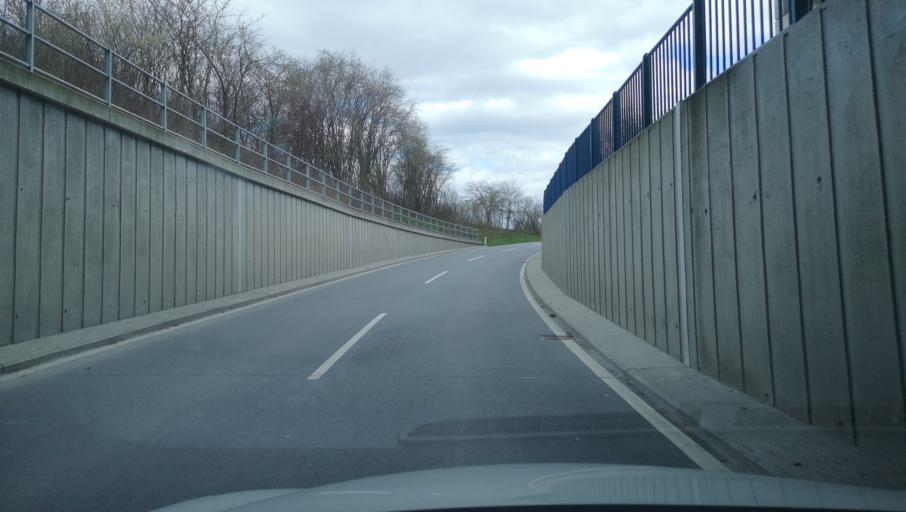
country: AT
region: Lower Austria
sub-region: Politischer Bezirk Melk
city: Blindenmarkt
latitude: 48.1251
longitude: 14.9741
